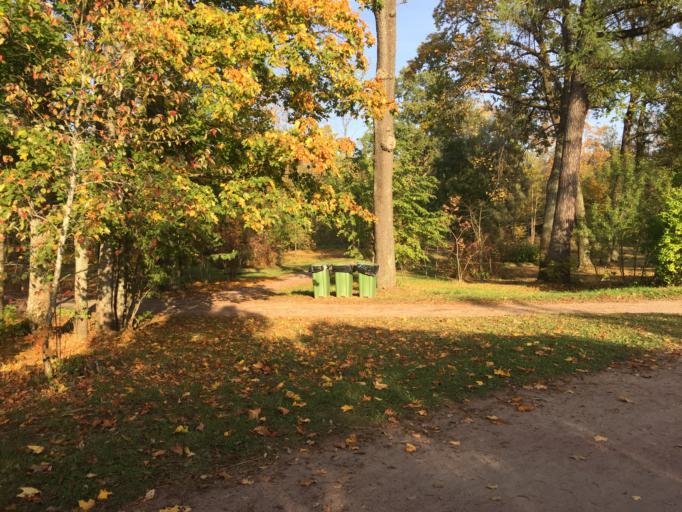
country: RU
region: St.-Petersburg
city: Pushkin
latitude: 59.7223
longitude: 30.3733
